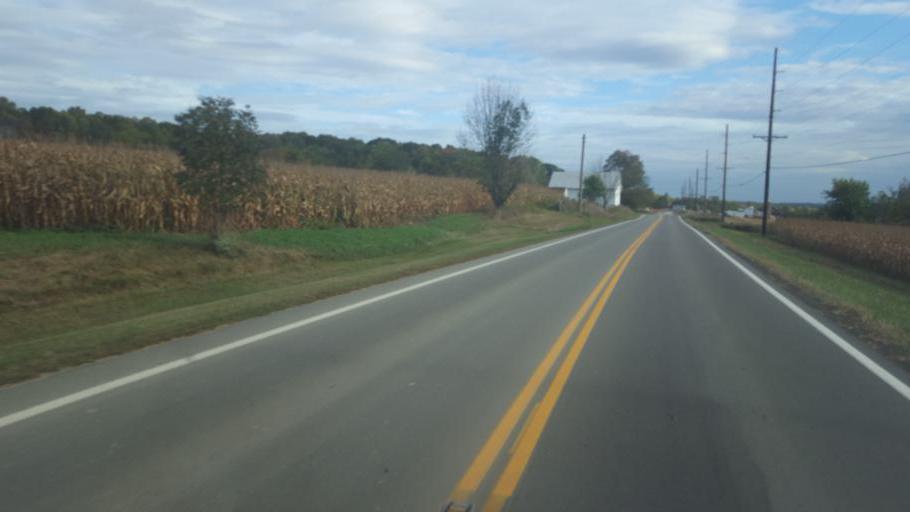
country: US
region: Ohio
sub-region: Ashland County
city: Ashland
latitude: 40.8162
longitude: -82.1993
